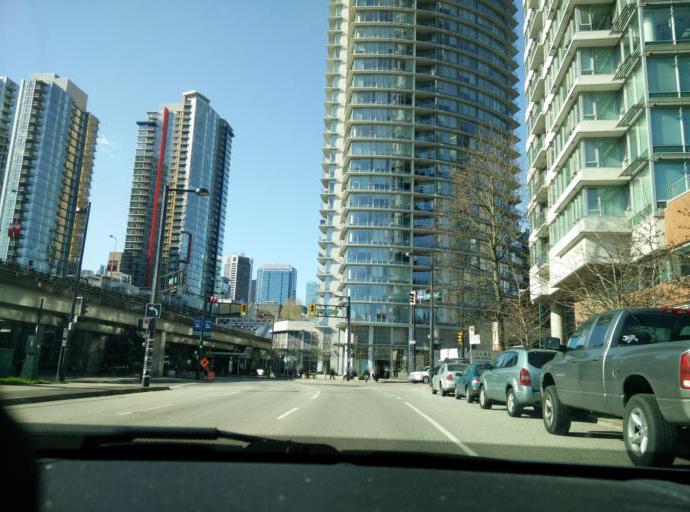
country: CA
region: British Columbia
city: West End
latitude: 49.2785
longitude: -123.1073
